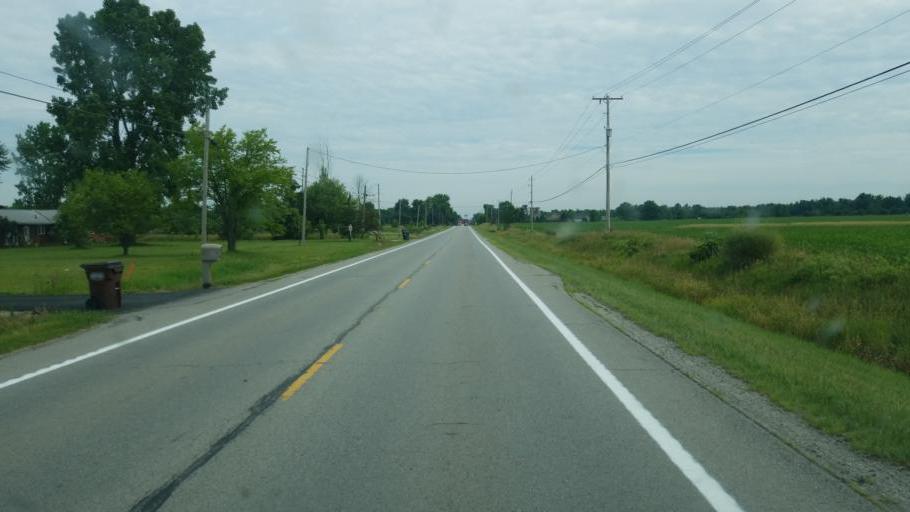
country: US
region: Ohio
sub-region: Lorain County
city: Grafton
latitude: 41.2499
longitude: -82.0227
